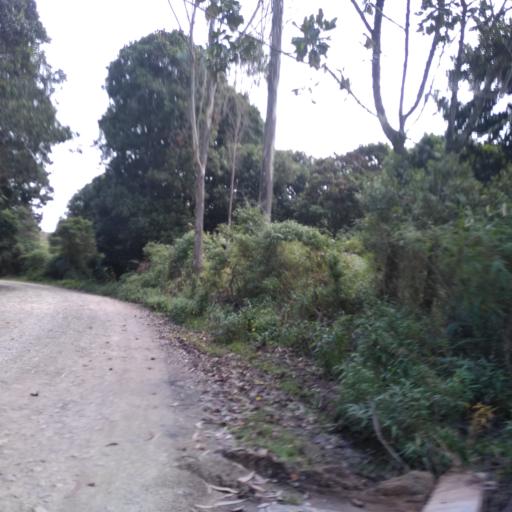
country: CO
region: Boyaca
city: Duitama
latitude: 5.9476
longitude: -73.1447
